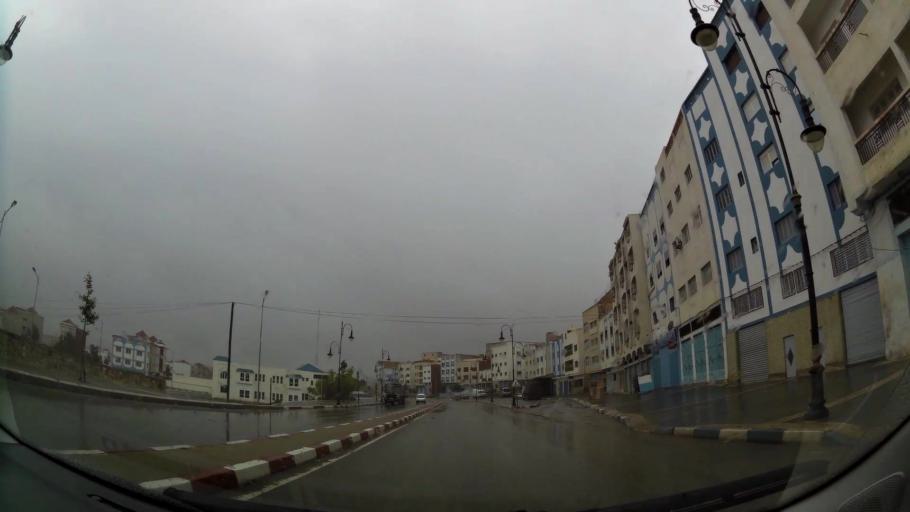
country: MA
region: Taza-Al Hoceima-Taounate
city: Imzourene
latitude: 35.1516
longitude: -3.8440
